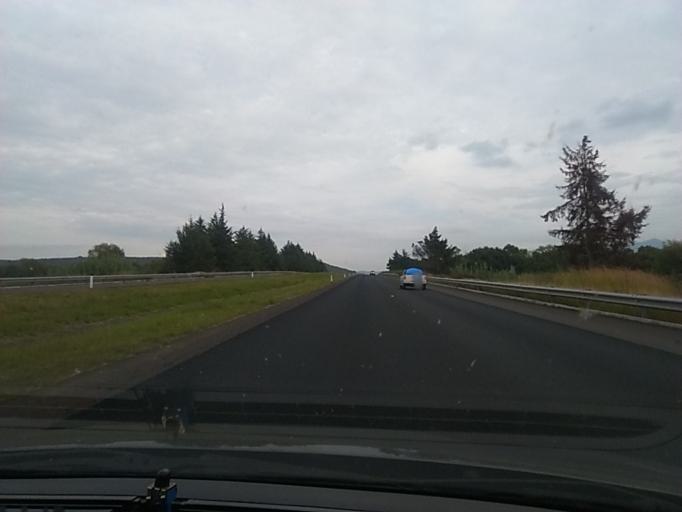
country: MX
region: Mexico
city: Huaniqueo de Morales
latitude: 19.9037
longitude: -101.5779
